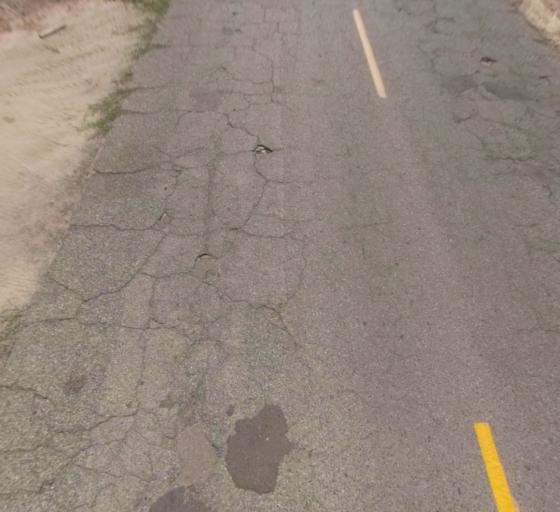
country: US
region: California
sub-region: Fresno County
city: Biola
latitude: 36.8368
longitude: -120.0808
